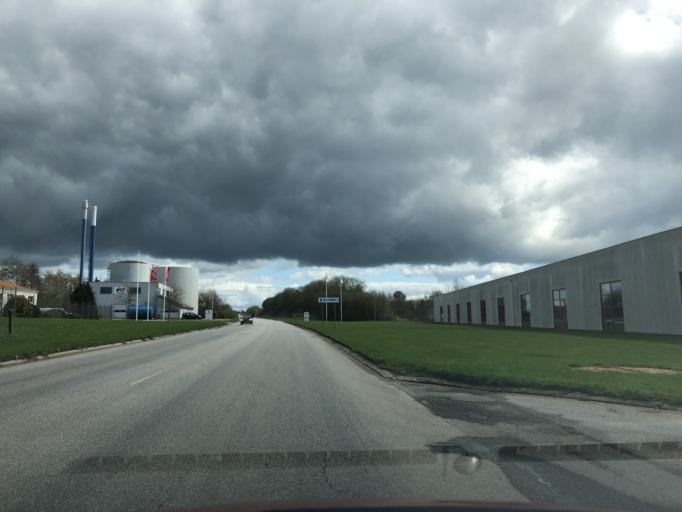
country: DK
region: South Denmark
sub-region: Kolding Kommune
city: Christiansfeld
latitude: 55.3638
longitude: 9.4872
